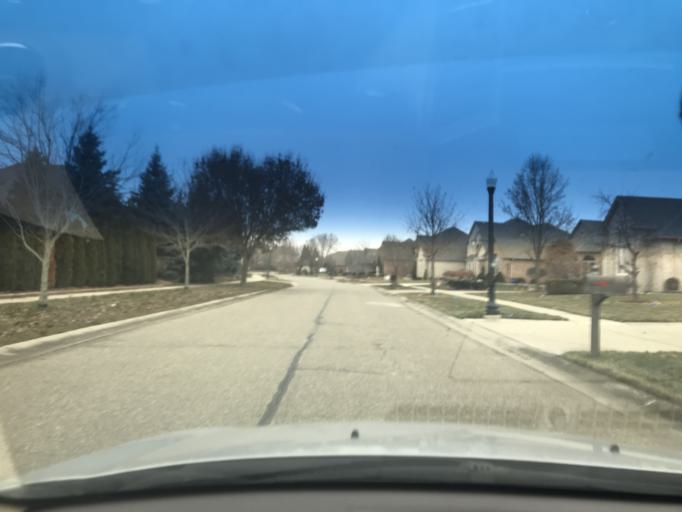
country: US
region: Michigan
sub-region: Macomb County
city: Shelby
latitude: 42.7091
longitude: -83.0404
